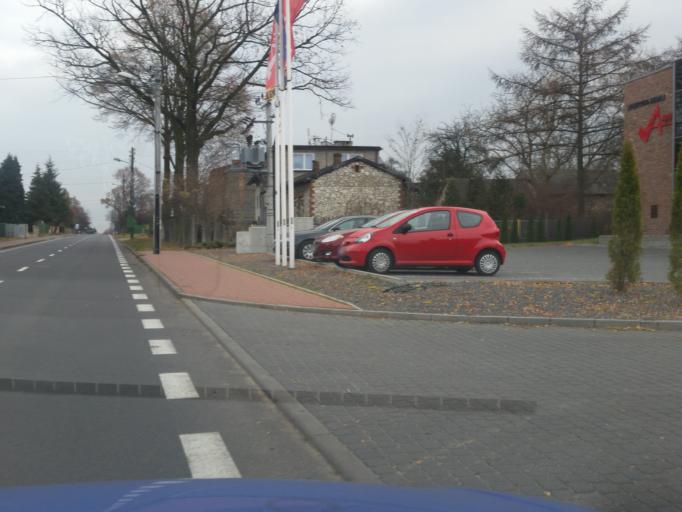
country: PL
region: Silesian Voivodeship
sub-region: Czestochowa
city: Czestochowa
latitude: 50.8163
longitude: 19.1760
